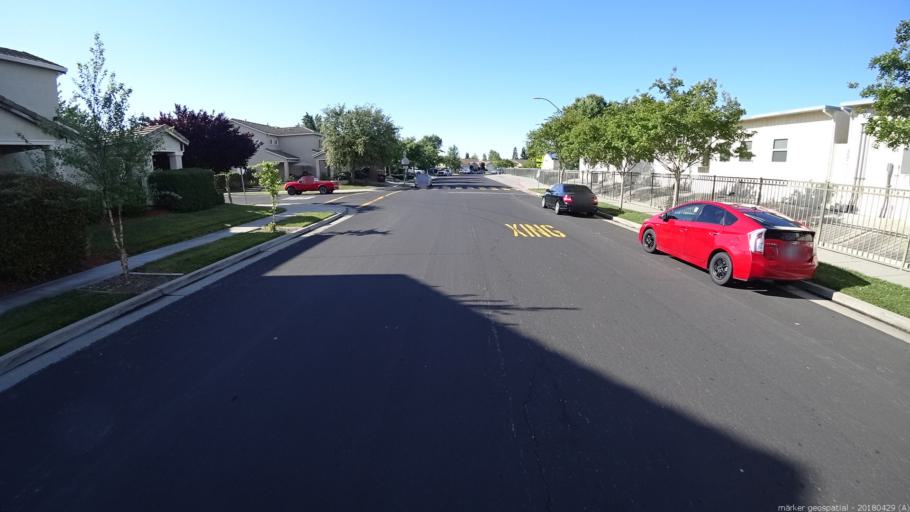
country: US
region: California
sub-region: Yolo County
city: West Sacramento
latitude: 38.5414
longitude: -121.5663
